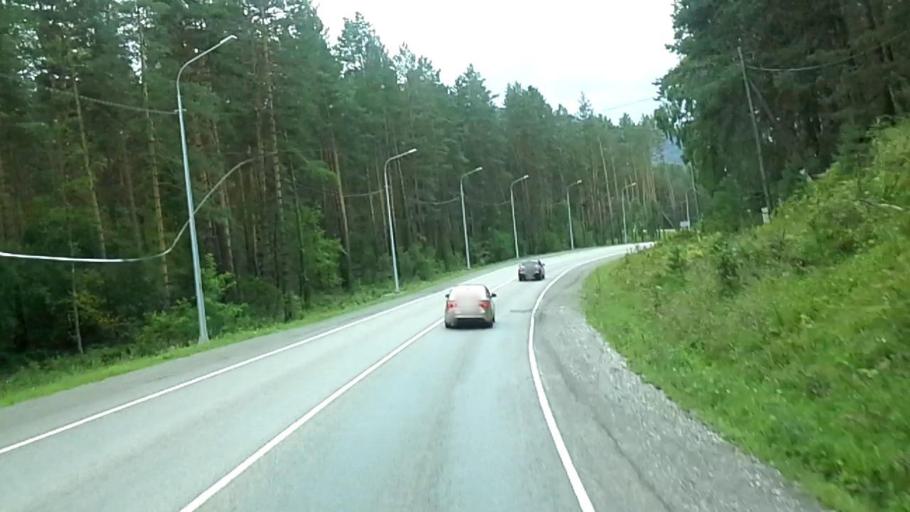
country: RU
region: Altay
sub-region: Mayminskiy Rayon
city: Manzherok
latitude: 51.8240
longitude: 85.7896
